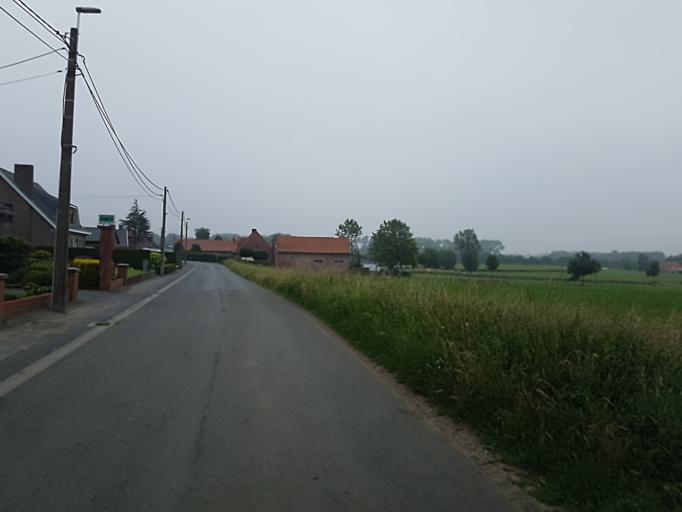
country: BE
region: Flanders
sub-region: Provincie West-Vlaanderen
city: Zonnebeke
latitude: 50.8672
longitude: 2.9839
